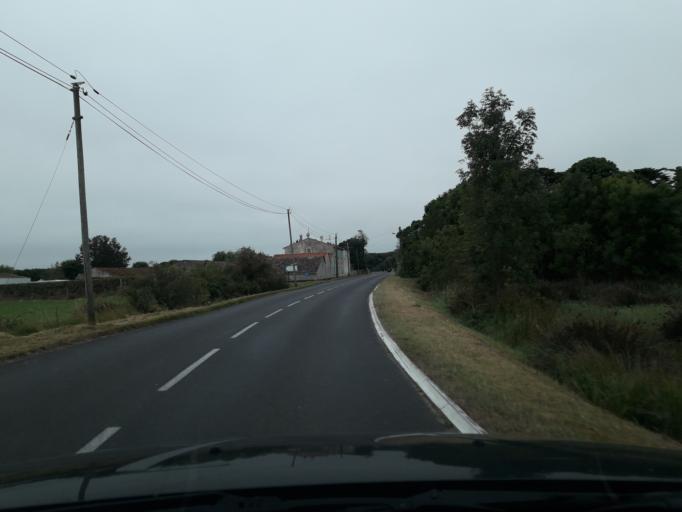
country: FR
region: Poitou-Charentes
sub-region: Departement de la Charente-Maritime
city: Boyard-Ville
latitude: 45.9542
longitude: -1.2490
